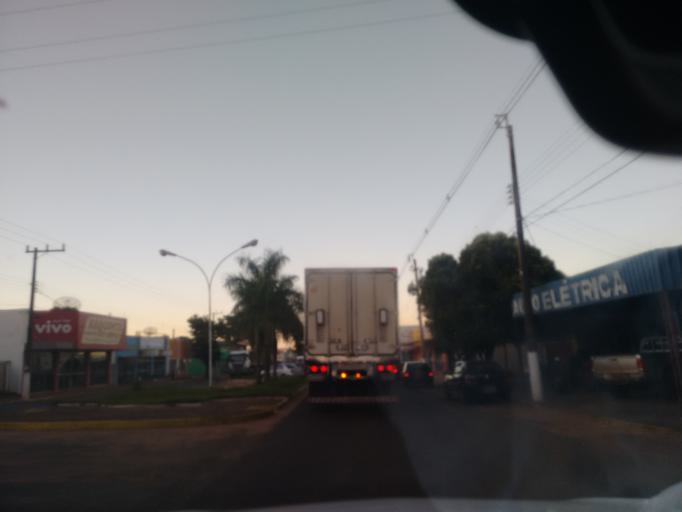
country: BR
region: Mato Grosso do Sul
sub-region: Eldorado
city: Eldorado
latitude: -23.4774
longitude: -54.1874
